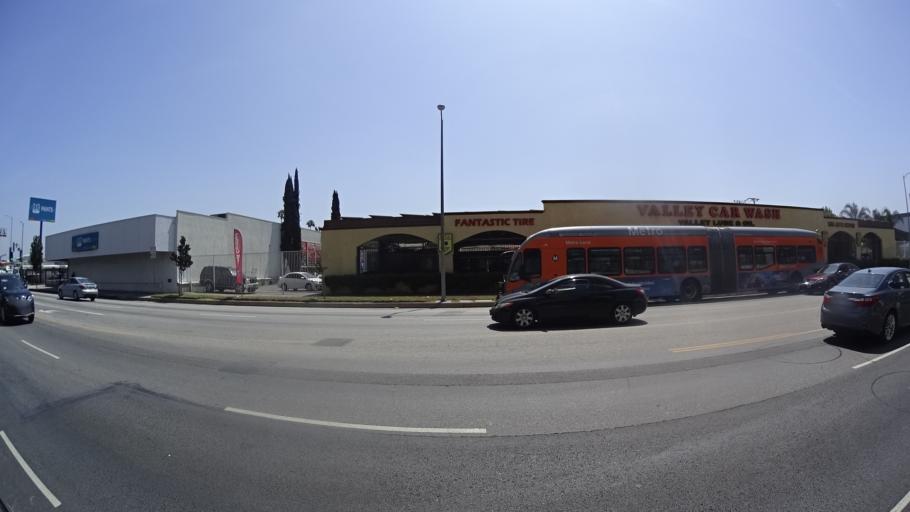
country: US
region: California
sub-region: Los Angeles County
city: Van Nuys
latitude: 34.2078
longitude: -118.4488
